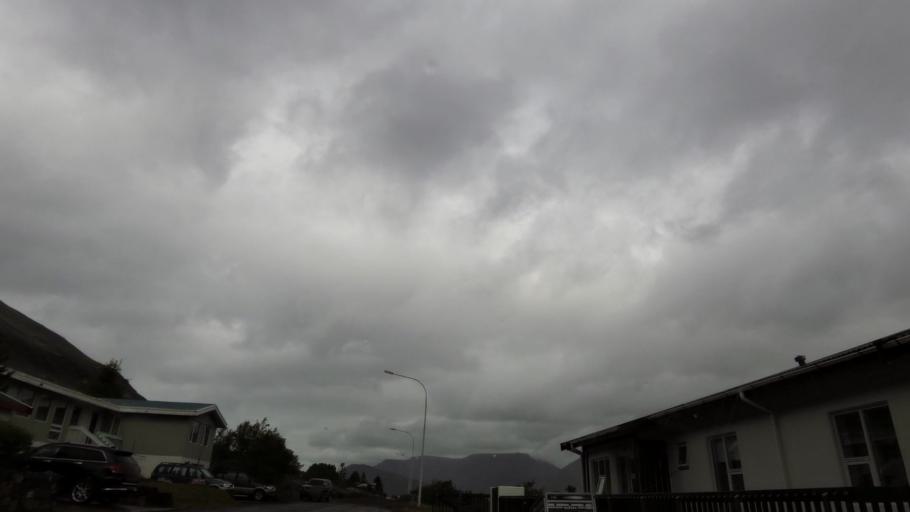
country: IS
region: Westfjords
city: Isafjoerdur
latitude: 65.8735
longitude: -23.4883
